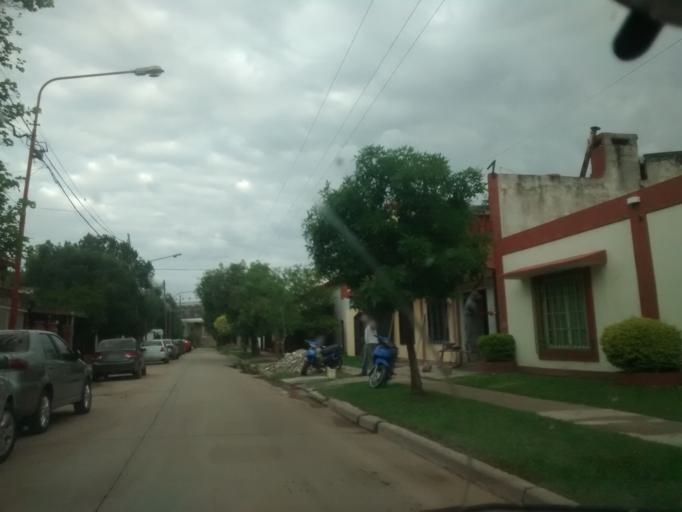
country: AR
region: Chaco
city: Fontana
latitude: -27.4432
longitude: -59.0157
